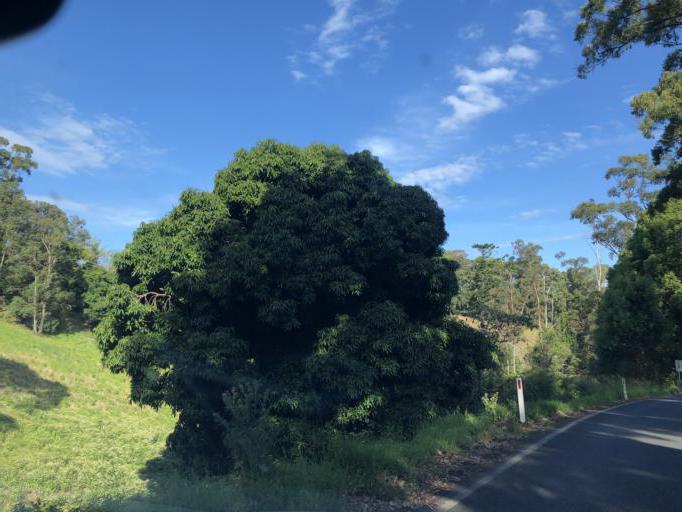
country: AU
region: New South Wales
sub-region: Coffs Harbour
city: Coffs Harbour
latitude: -30.2619
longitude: 153.1307
